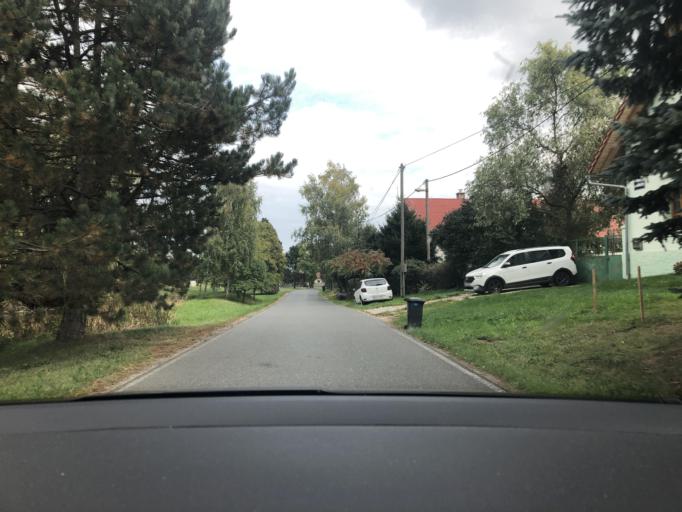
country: CZ
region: Central Bohemia
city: Zizelice
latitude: 50.1056
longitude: 15.4237
